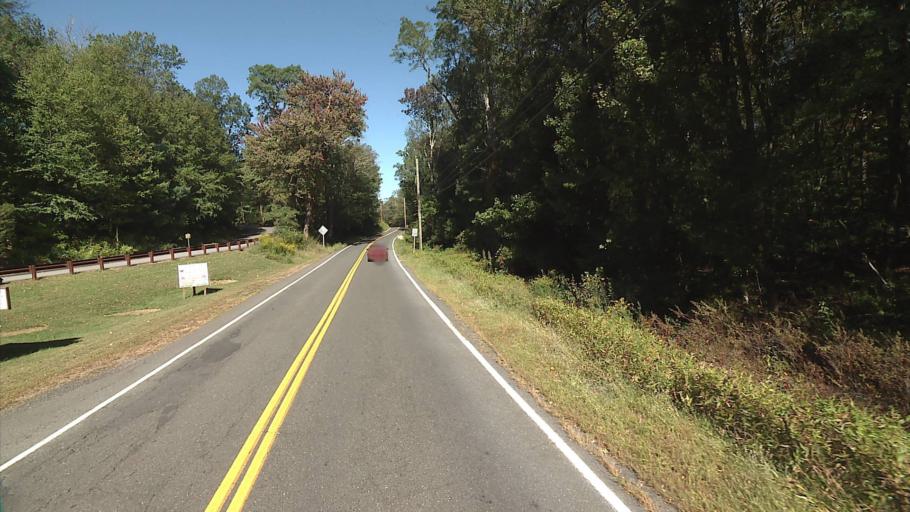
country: US
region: Connecticut
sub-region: Hartford County
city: Bristol
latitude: 41.7331
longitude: -72.9539
